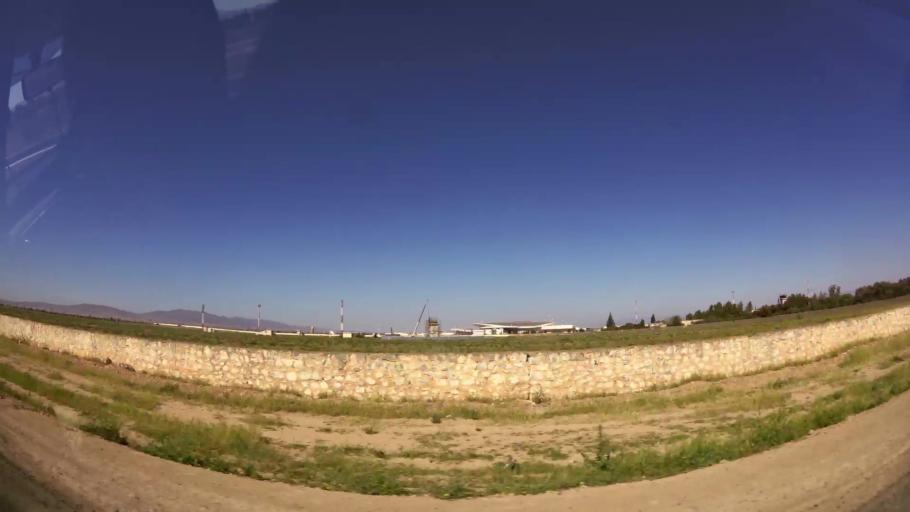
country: MA
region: Oriental
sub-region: Oujda-Angad
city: Oujda
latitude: 34.7850
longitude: -1.9488
